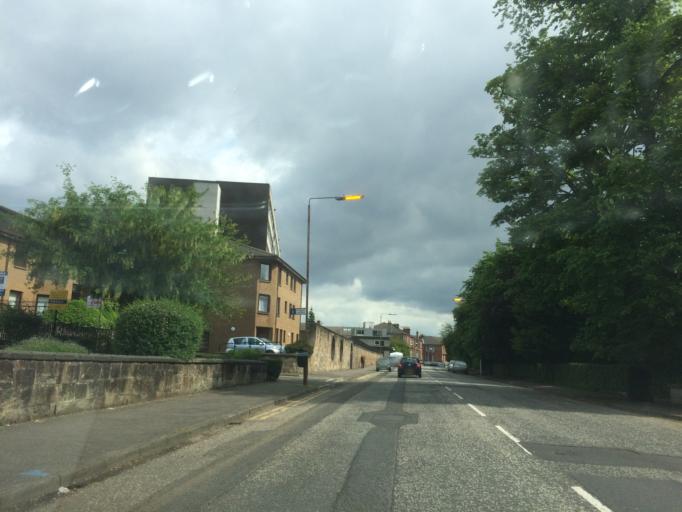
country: GB
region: Scotland
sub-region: East Renfrewshire
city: Giffnock
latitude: 55.8252
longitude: -4.2741
